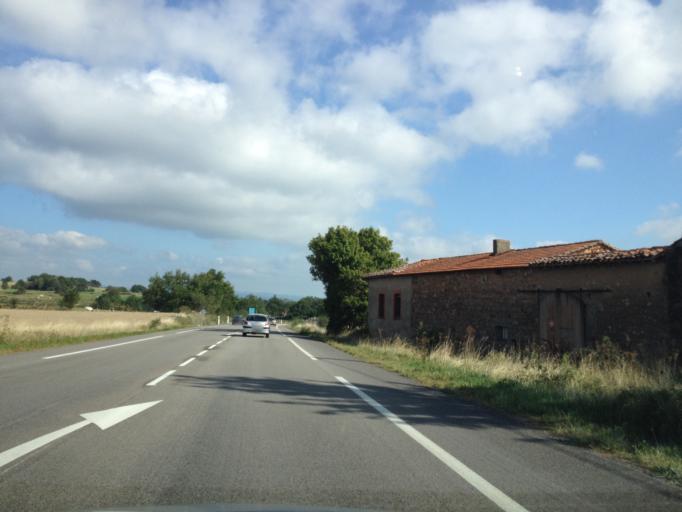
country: FR
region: Rhone-Alpes
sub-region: Departement de la Loire
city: Saint-Germain-Laval
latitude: 45.9059
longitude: 4.0083
